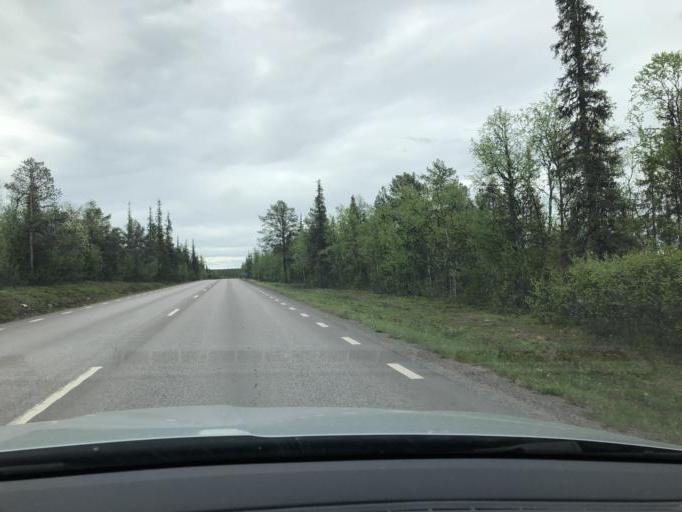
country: SE
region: Norrbotten
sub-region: Kiruna Kommun
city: Kiruna
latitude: 67.8185
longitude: 20.5668
